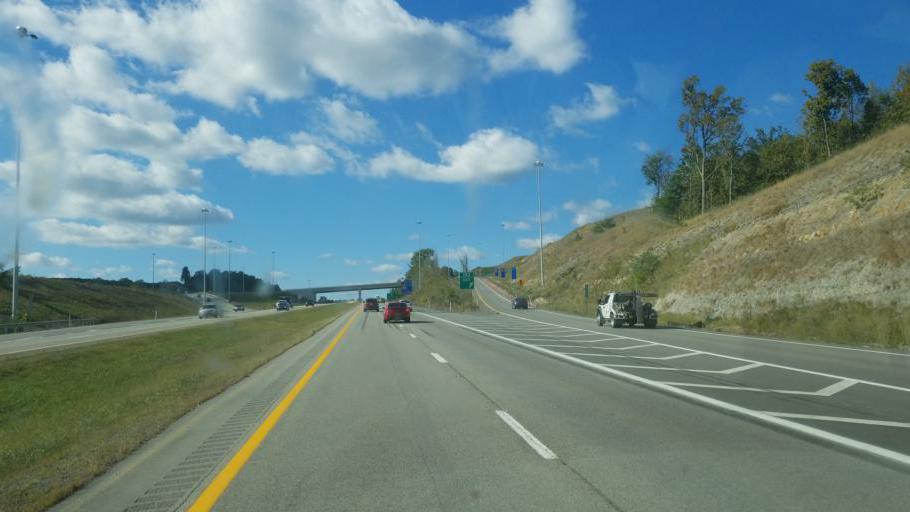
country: US
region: West Virginia
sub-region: Monongalia County
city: Star City
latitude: 39.6358
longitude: -79.9971
